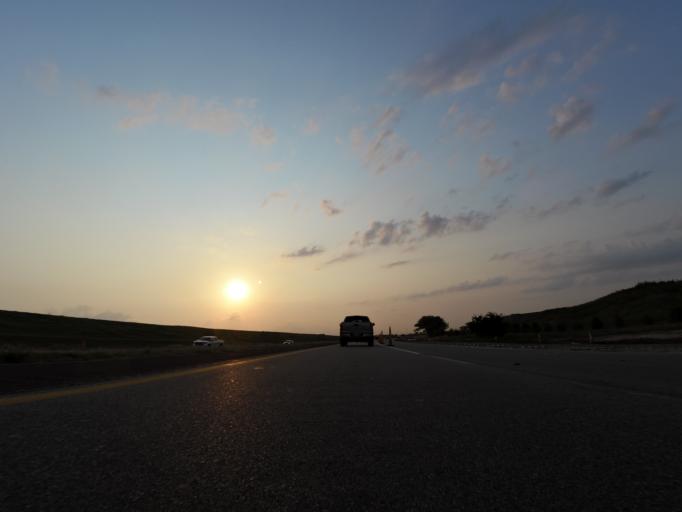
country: US
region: Kansas
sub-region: Sedgwick County
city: Maize
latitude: 37.7594
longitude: -97.3993
